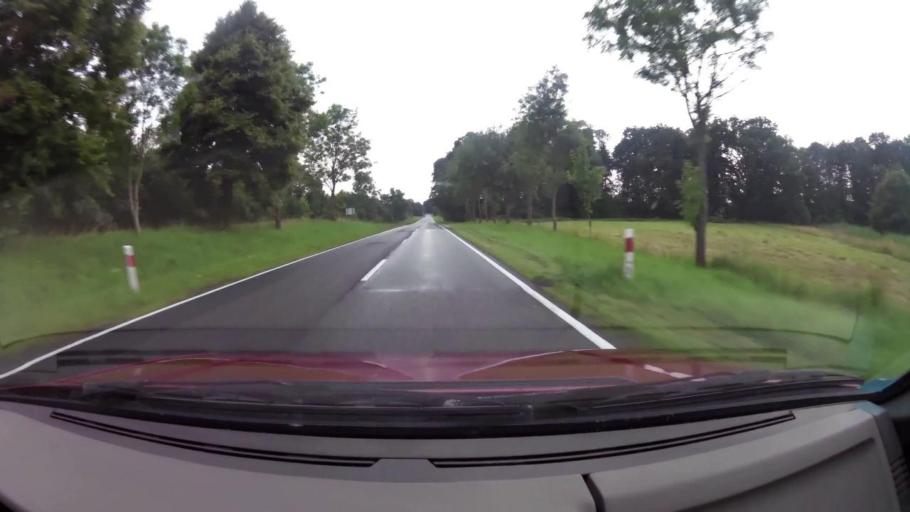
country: PL
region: West Pomeranian Voivodeship
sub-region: Powiat lobeski
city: Wegorzyno
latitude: 53.5232
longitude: 15.5121
